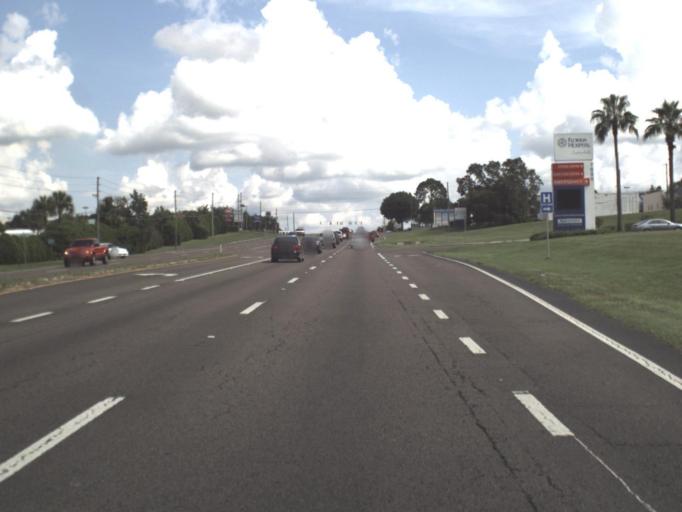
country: US
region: Florida
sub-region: Pasco County
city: Zephyrhills North
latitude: 28.2601
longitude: -82.1880
